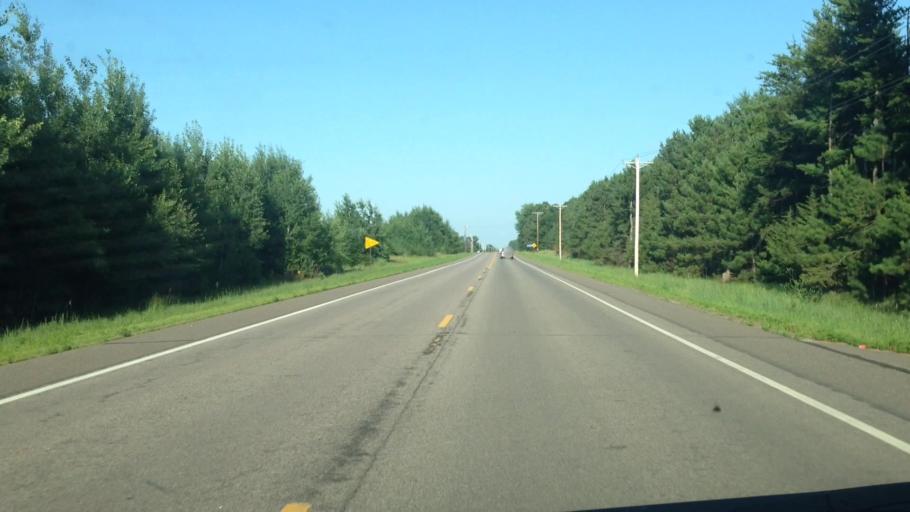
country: US
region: Minnesota
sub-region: Sherburne County
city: Big Lake
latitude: 45.4477
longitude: -93.7313
